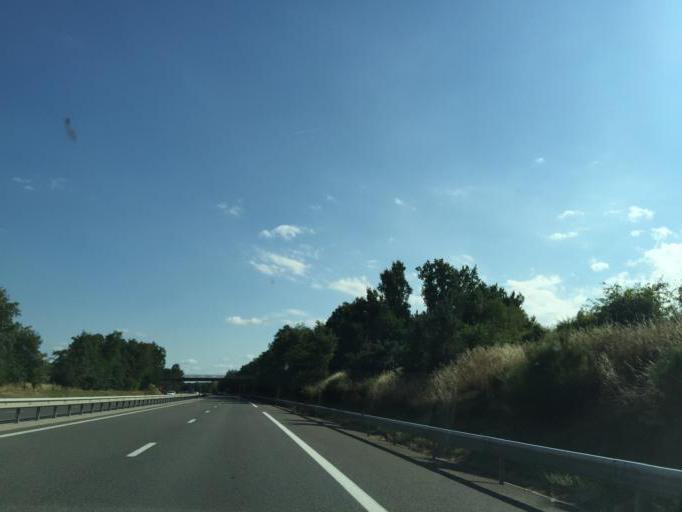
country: FR
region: Rhone-Alpes
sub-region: Departement de la Loire
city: Feurs
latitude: 45.6928
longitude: 4.1571
